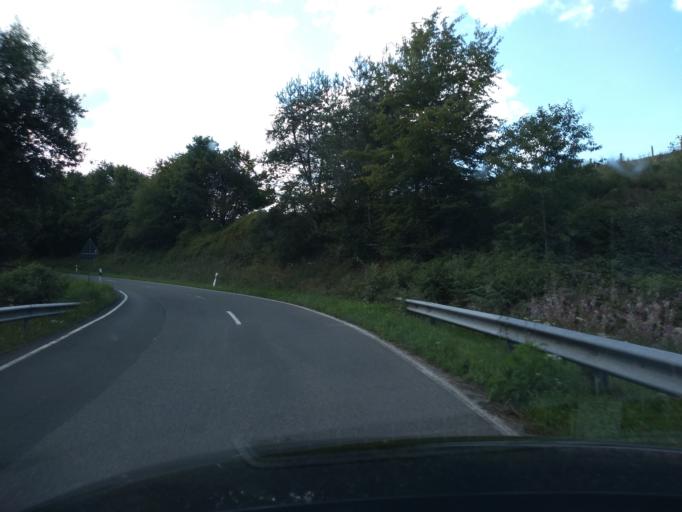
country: DE
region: North Rhine-Westphalia
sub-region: Regierungsbezirk Koln
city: Much
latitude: 50.8458
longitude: 7.4054
